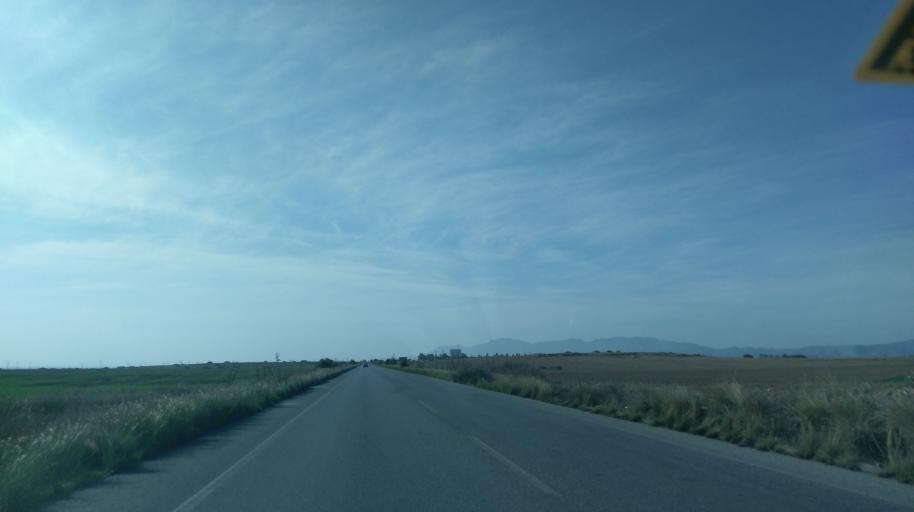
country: CY
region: Ammochostos
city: Lefkonoiko
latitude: 35.2612
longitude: 33.7715
